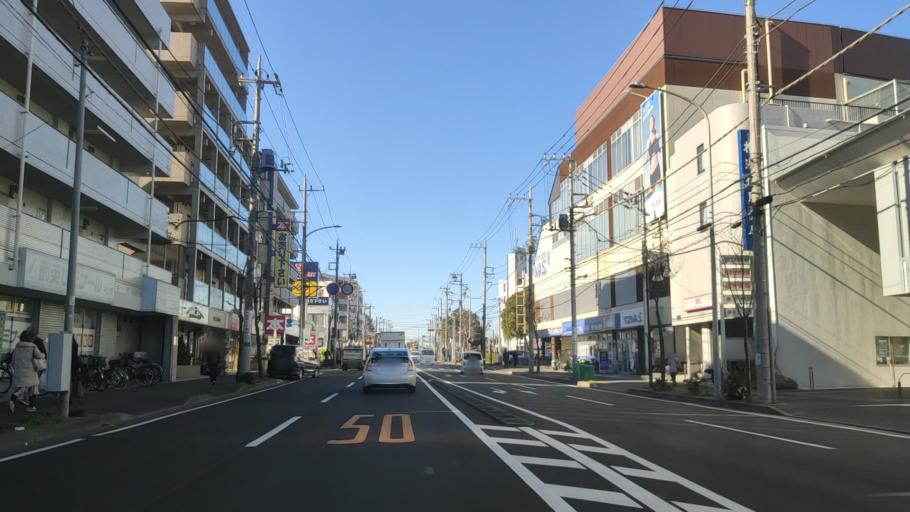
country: JP
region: Tokyo
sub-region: Machida-shi
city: Machida
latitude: 35.5148
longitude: 139.5364
